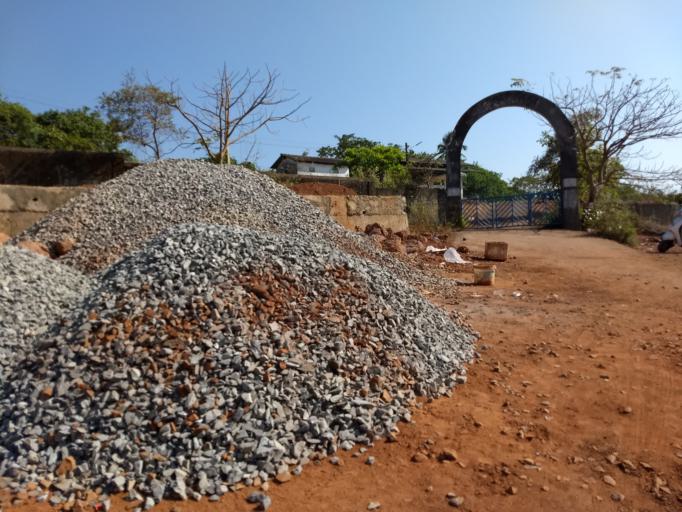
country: IN
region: Goa
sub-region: North Goa
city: Vagator
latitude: 15.6033
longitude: 73.7371
